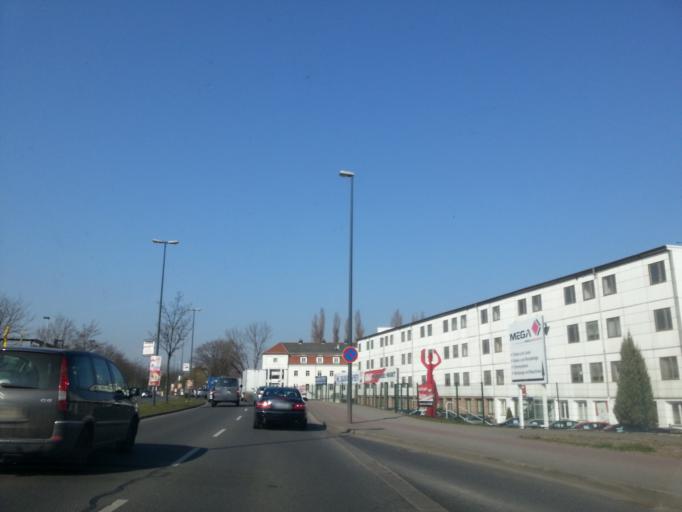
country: DE
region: Saxony
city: Dresden
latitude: 51.0131
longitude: 13.7773
